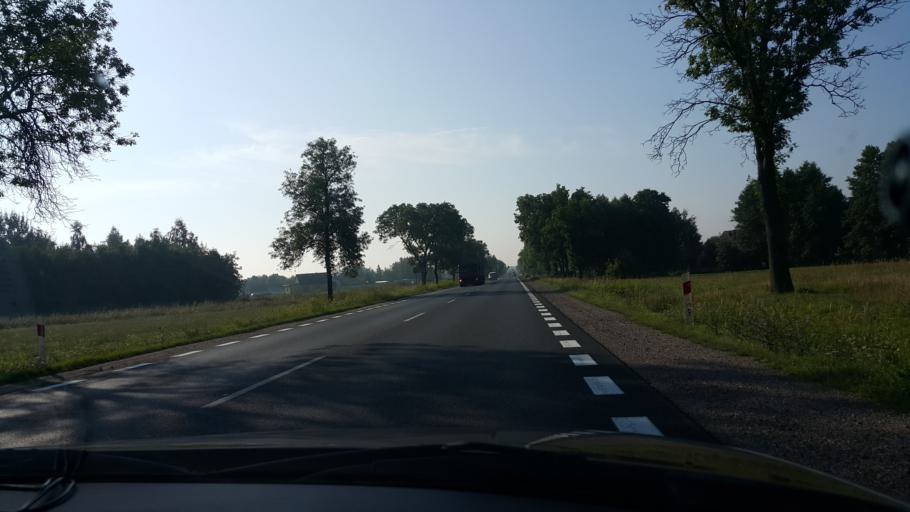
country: PL
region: Masovian Voivodeship
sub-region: Powiat radomski
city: Jedlnia-Letnisko
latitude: 51.3956
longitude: 21.2647
